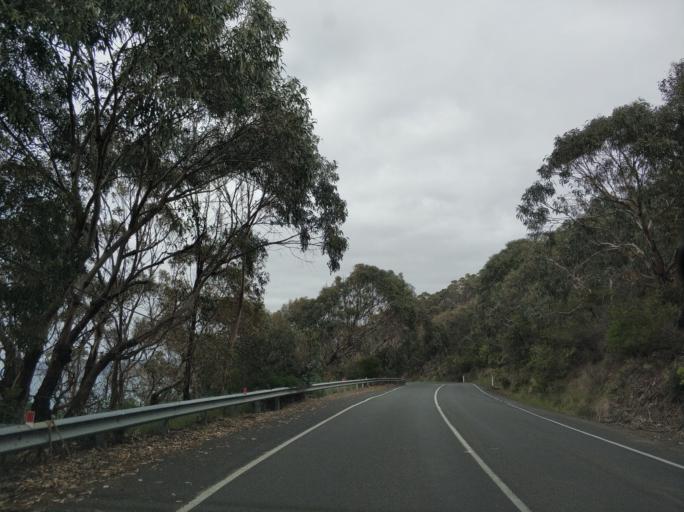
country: AU
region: Victoria
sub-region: Surf Coast
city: Anglesea
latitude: -38.4871
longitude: 144.0272
